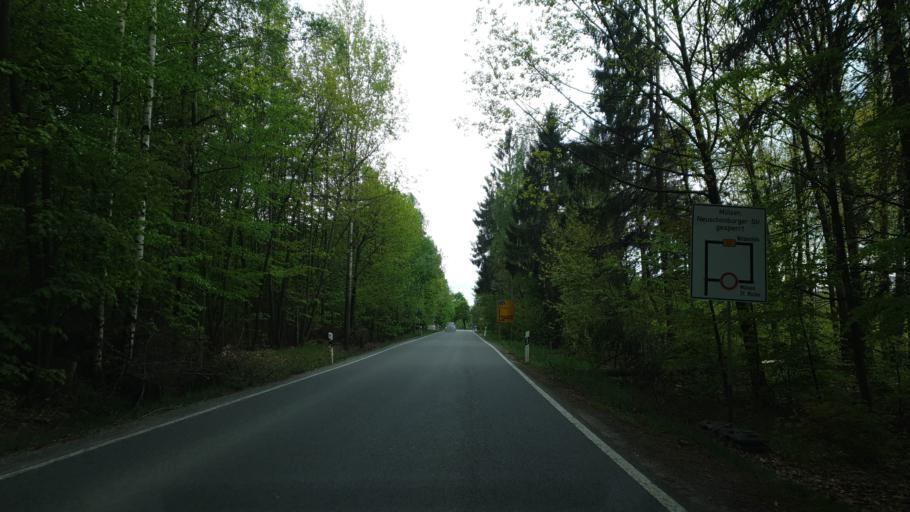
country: DE
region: Saxony
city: Oelsnitz
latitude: 50.7138
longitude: 12.6647
